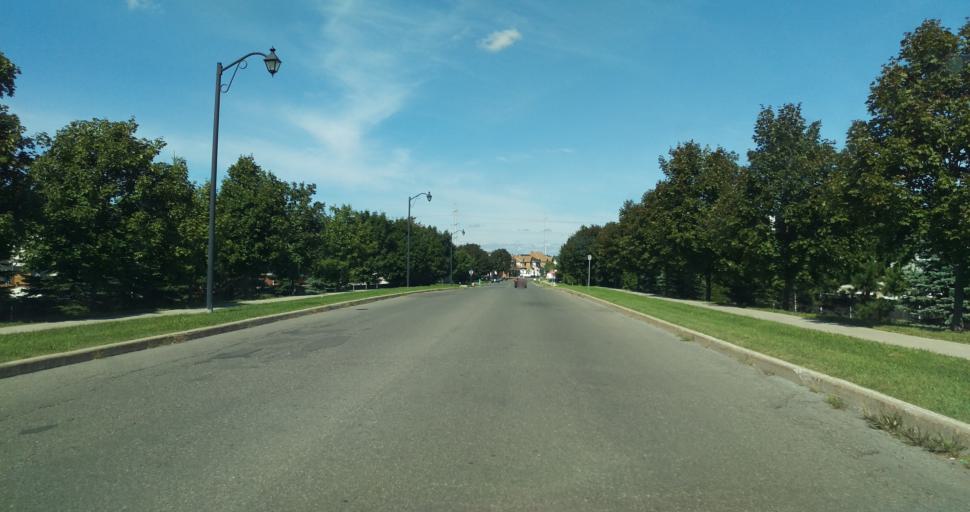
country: CA
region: Ontario
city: Clarence-Rockland
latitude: 45.4588
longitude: -75.4757
